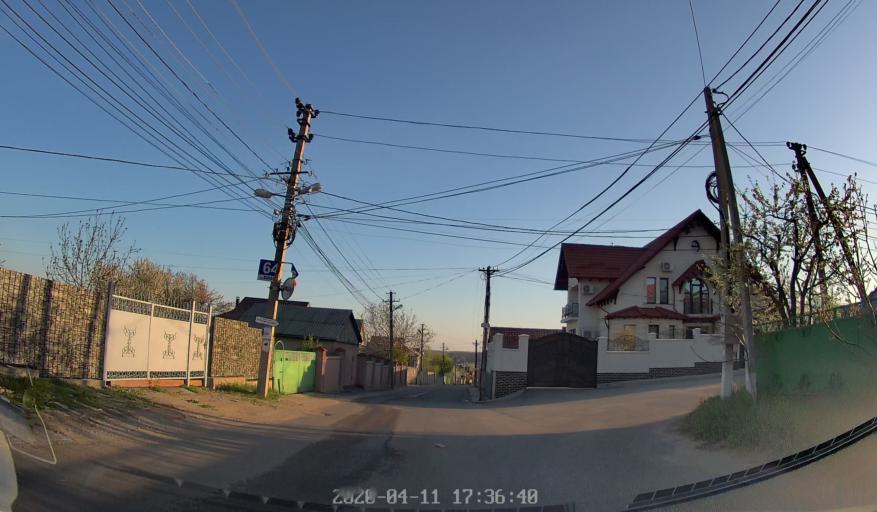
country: MD
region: Laloveni
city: Ialoveni
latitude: 46.9830
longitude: 28.8034
